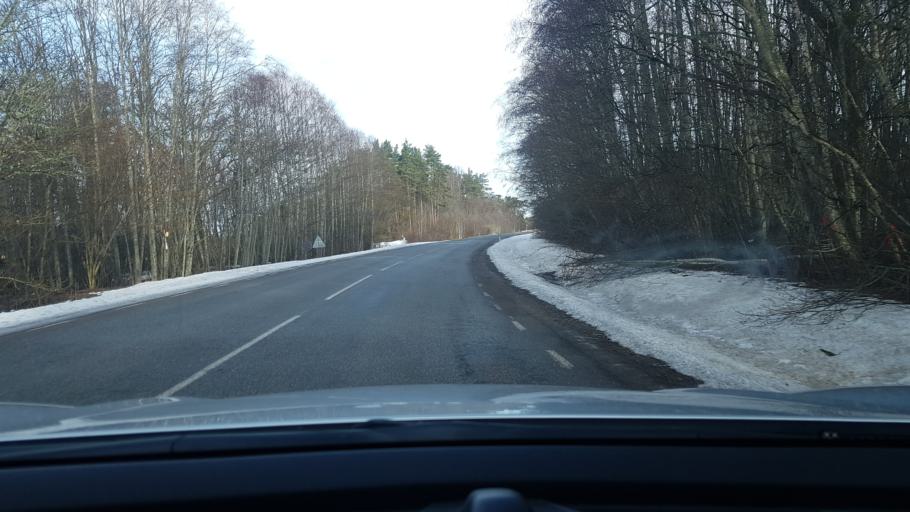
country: EE
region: Saare
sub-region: Kuressaare linn
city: Kuressaare
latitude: 58.3993
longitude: 22.6427
